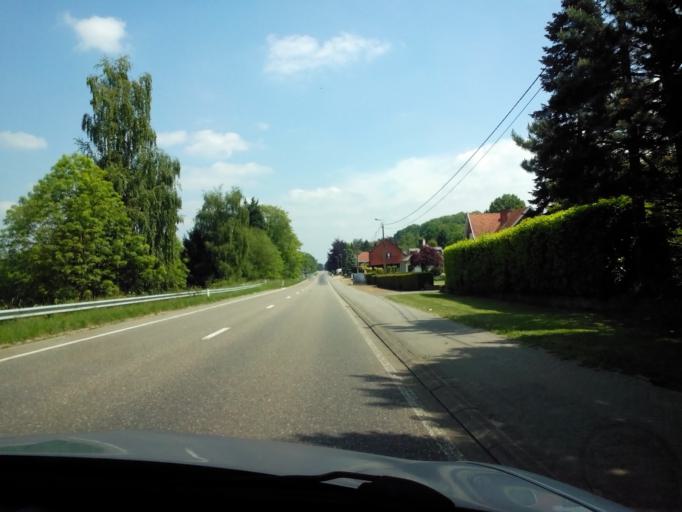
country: BE
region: Flanders
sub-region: Provincie Vlaams-Brabant
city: Aarschot
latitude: 50.9704
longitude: 4.7970
